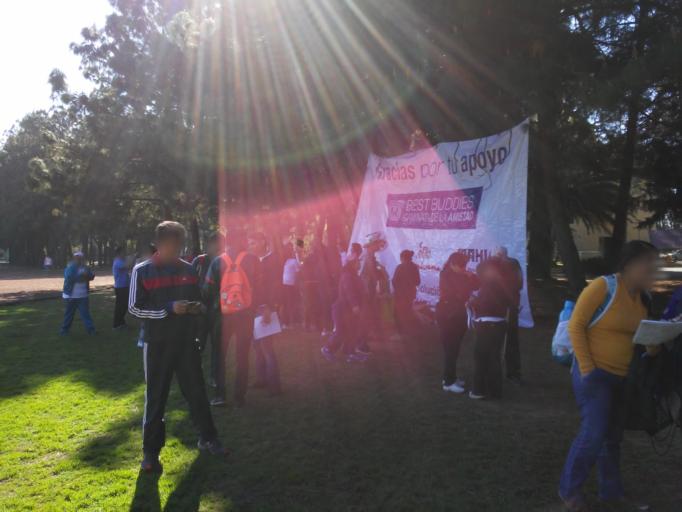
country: MX
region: Mexico
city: Toluca
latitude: 19.2704
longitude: -99.6542
